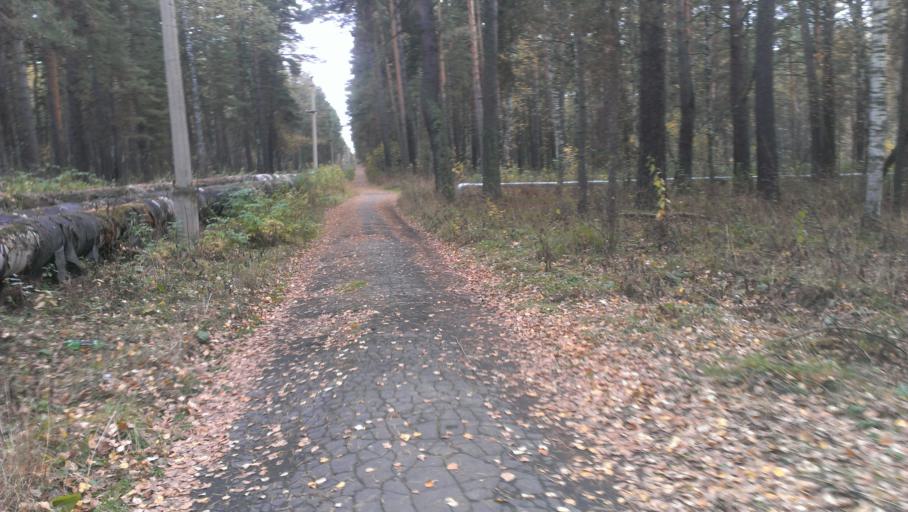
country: RU
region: Altai Krai
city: Yuzhnyy
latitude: 53.2689
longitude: 83.6820
